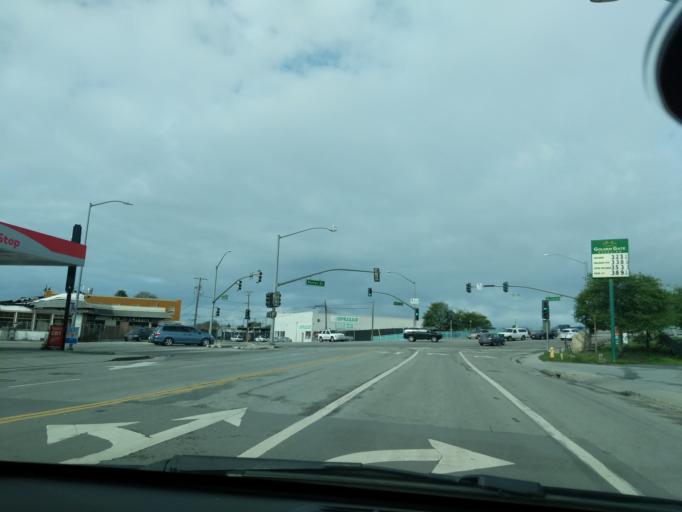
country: US
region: California
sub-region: Monterey County
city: Pajaro
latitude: 36.9045
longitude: -121.7497
